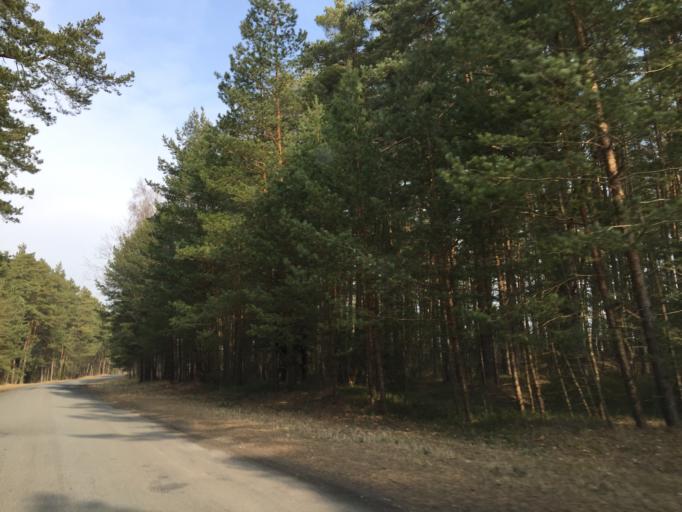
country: LV
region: Salacgrivas
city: Ainazi
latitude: 57.8982
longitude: 24.3743
